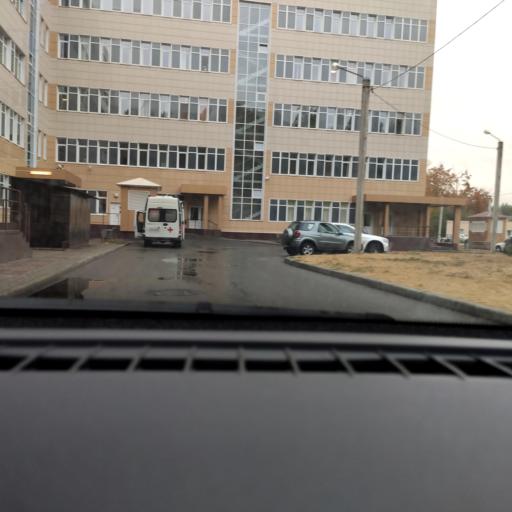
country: RU
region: Voronezj
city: Podgornoye
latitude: 51.7410
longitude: 39.1765
